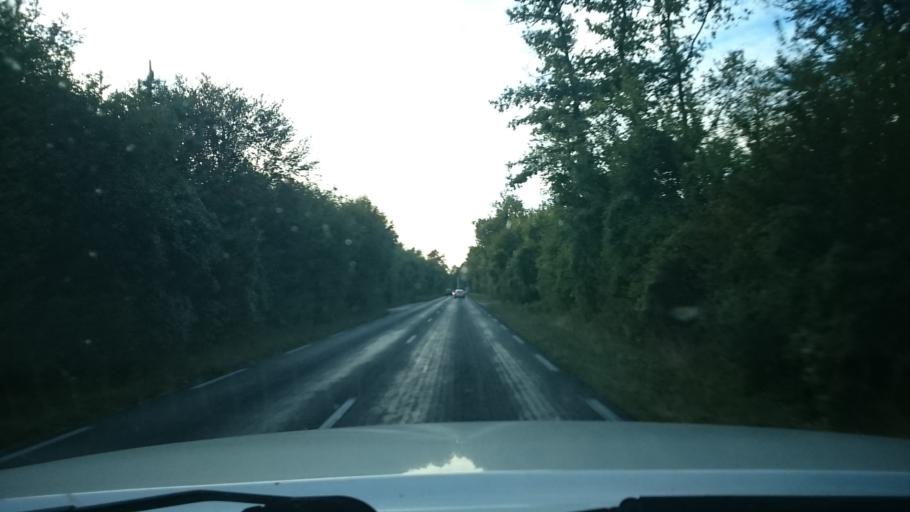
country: FR
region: Ile-de-France
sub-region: Departement de Seine-et-Marne
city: Samois-sur-Seine
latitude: 48.4415
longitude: 2.7237
